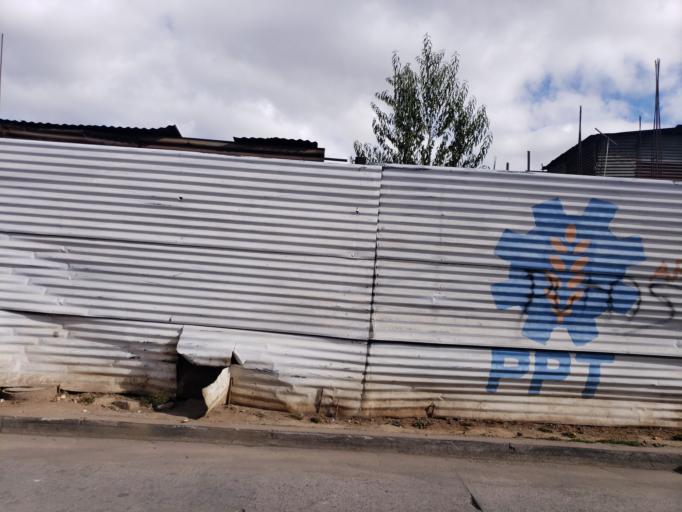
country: GT
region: Quetzaltenango
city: Ostuncalco
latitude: 14.8651
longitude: -91.6226
